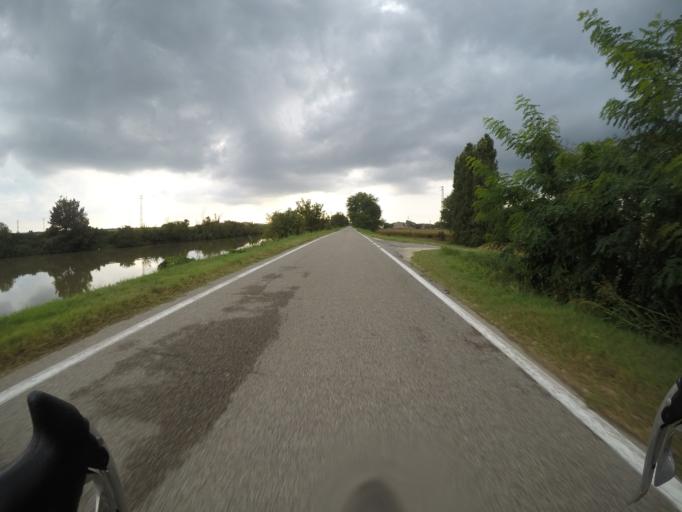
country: IT
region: Veneto
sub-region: Provincia di Rovigo
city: Arqua Polesine
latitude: 44.9963
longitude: 11.7240
